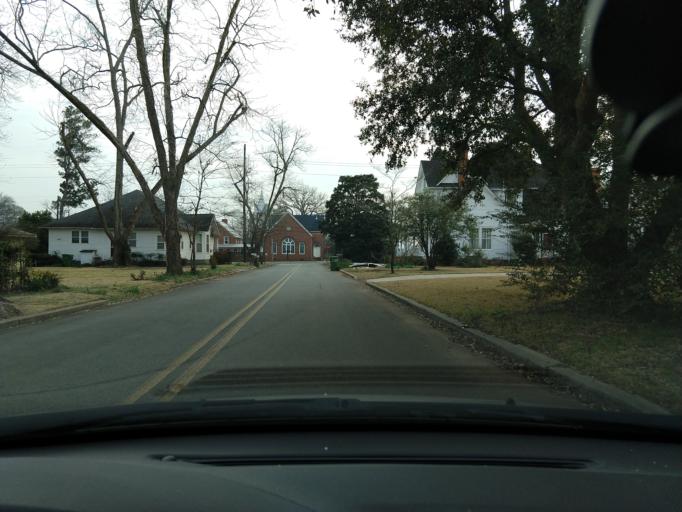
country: US
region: Georgia
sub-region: Webster County
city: Preston
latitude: 32.0348
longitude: -84.3980
